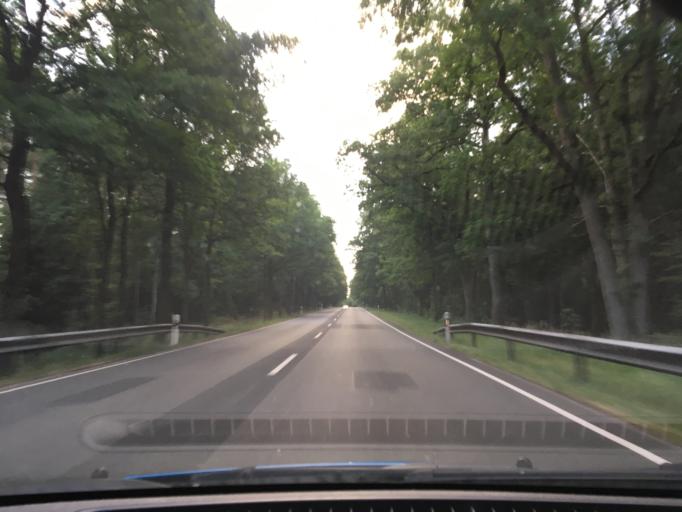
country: DE
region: Lower Saxony
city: Sprakensehl
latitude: 52.7347
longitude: 10.4862
